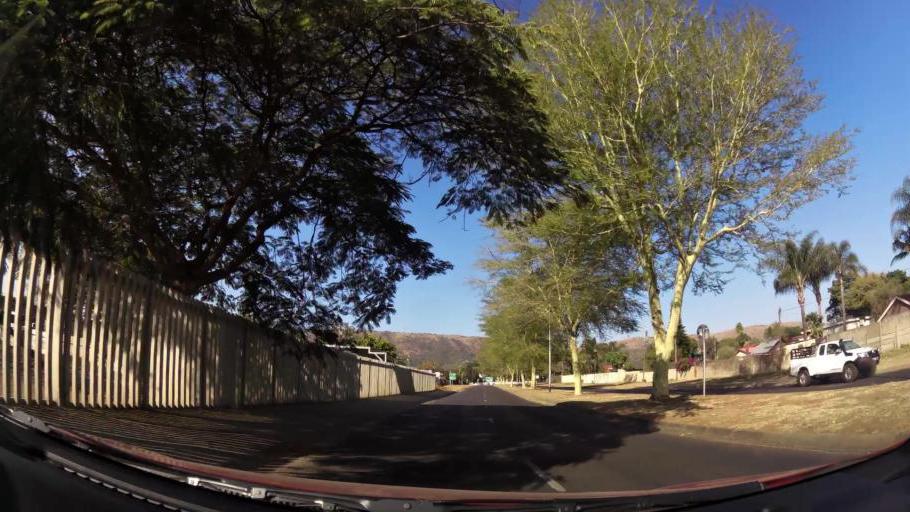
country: ZA
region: Gauteng
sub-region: City of Tshwane Metropolitan Municipality
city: Pretoria
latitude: -25.6748
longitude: 28.1653
